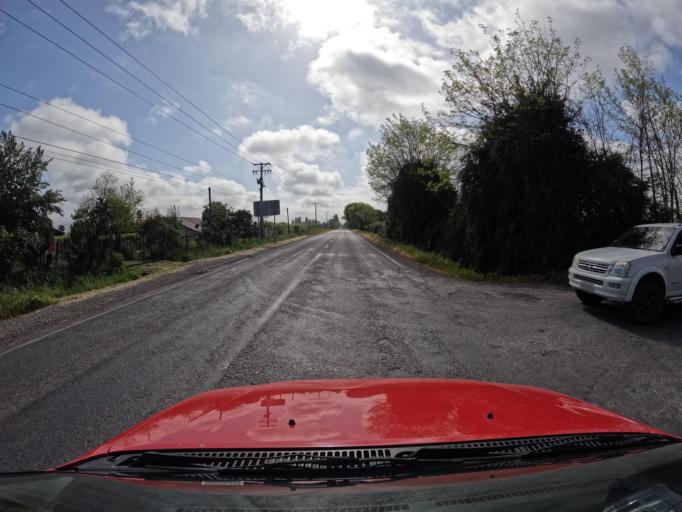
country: CL
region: Maule
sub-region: Provincia de Curico
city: Teno
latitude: -34.8647
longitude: -71.2038
